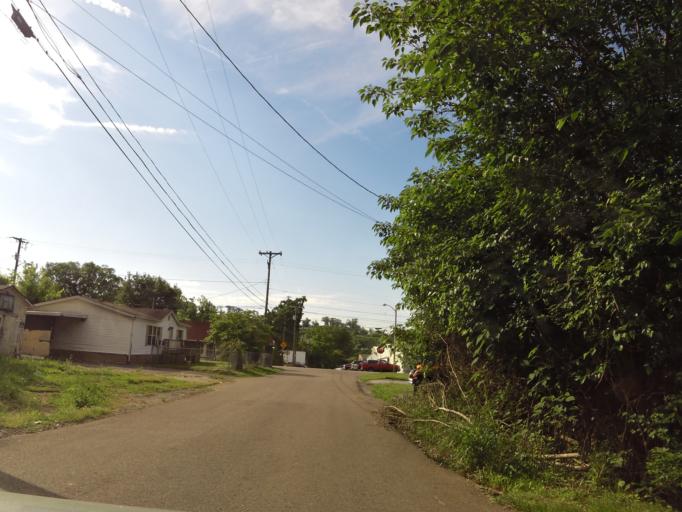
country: US
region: Tennessee
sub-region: Knox County
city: Knoxville
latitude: 35.9940
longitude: -83.9090
